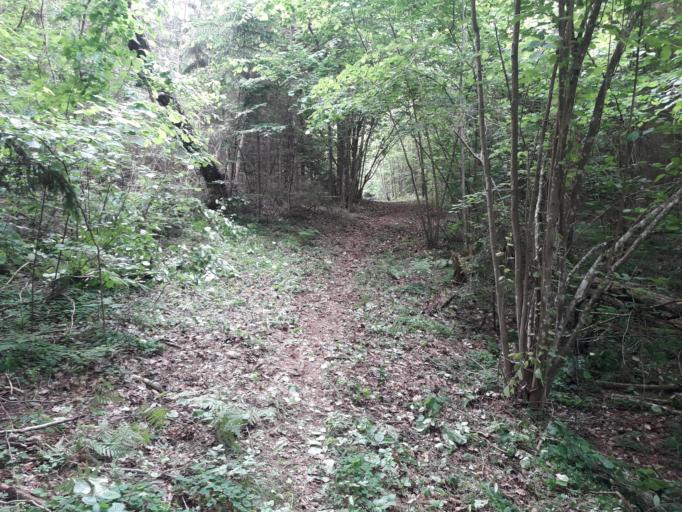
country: LT
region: Alytaus apskritis
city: Druskininkai
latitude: 54.1206
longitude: 23.9858
